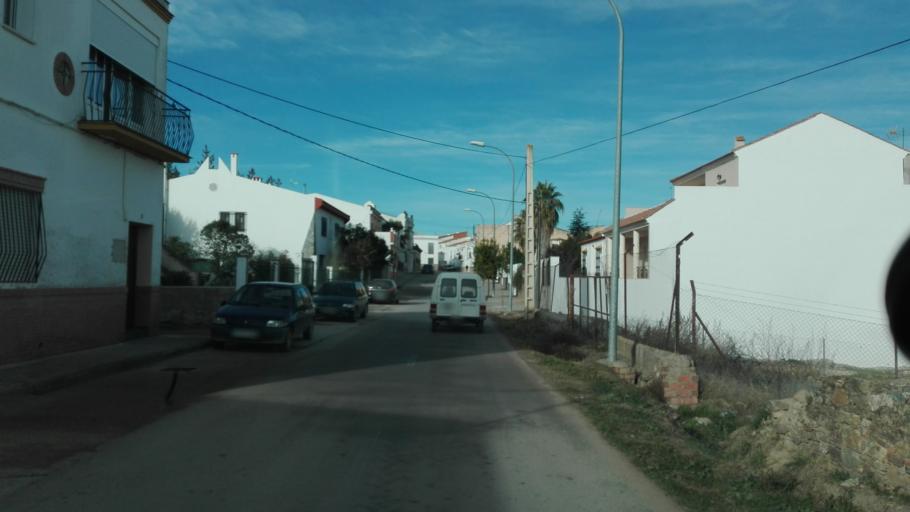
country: ES
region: Extremadura
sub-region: Provincia de Badajoz
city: Usagre
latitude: 38.3578
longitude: -6.1612
